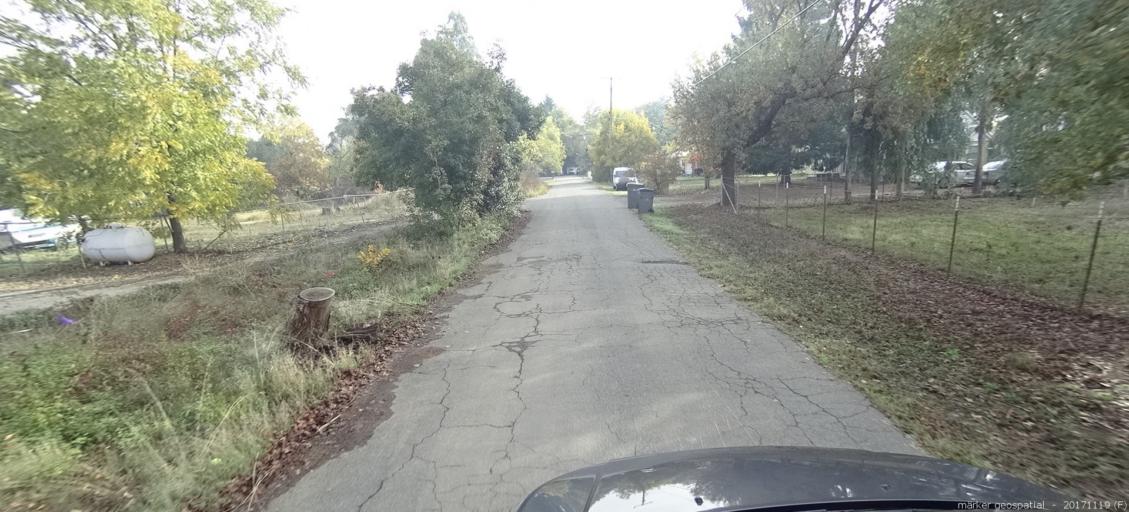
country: US
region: California
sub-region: Shasta County
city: Redding
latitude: 40.5188
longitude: -122.3480
